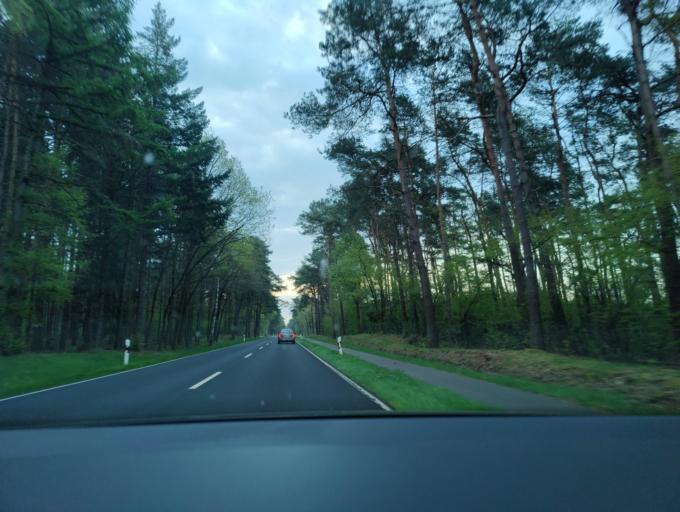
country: DE
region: Lower Saxony
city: Emsburen
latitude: 52.4592
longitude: 7.2844
